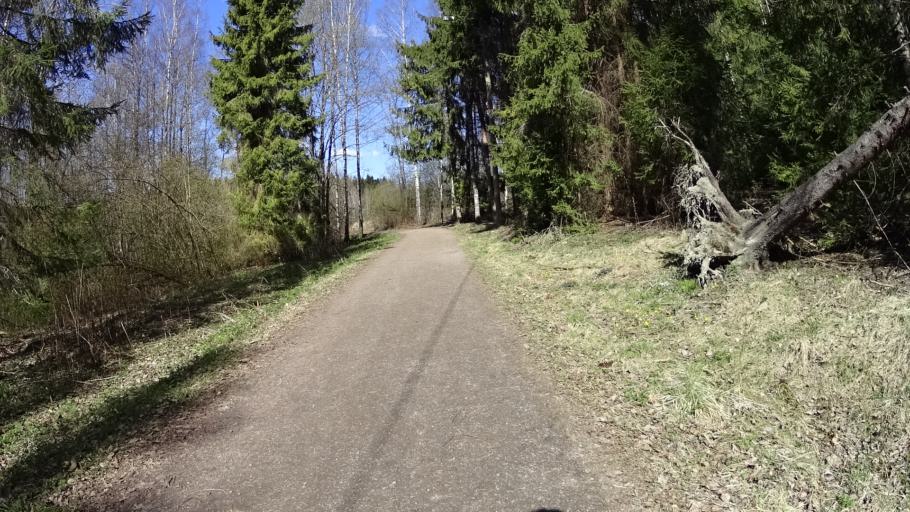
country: FI
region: Uusimaa
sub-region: Helsinki
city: Espoo
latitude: 60.2396
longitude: 24.6513
